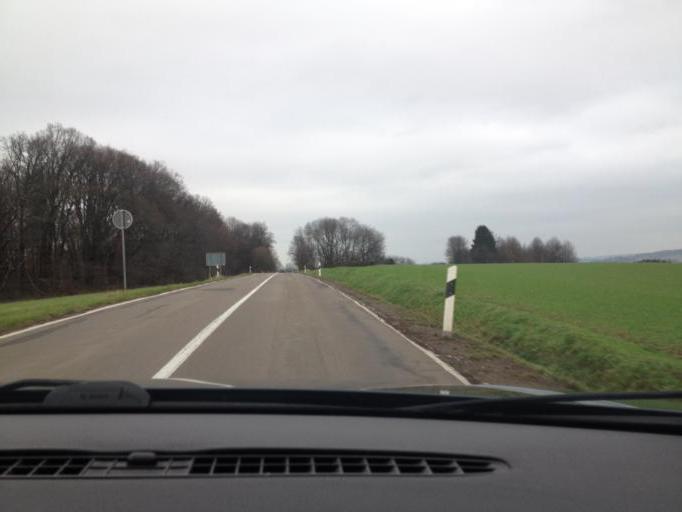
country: DE
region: Saarland
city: Mainzweiler
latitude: 49.3947
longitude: 7.1344
